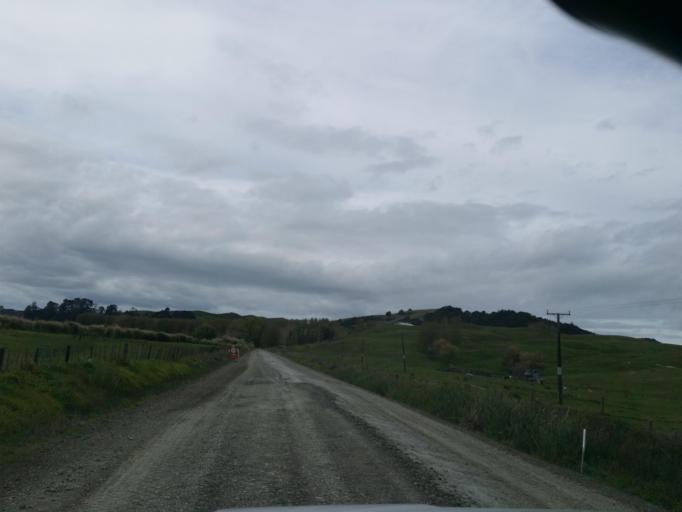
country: NZ
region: Northland
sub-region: Kaipara District
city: Dargaville
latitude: -35.9283
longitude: 173.9207
